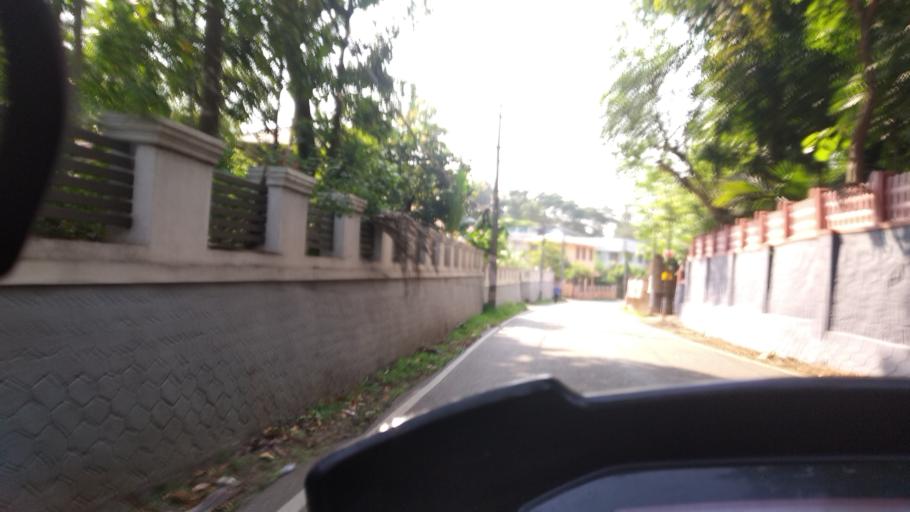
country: IN
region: Kerala
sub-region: Ernakulam
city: Piravam
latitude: 9.8713
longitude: 76.4985
